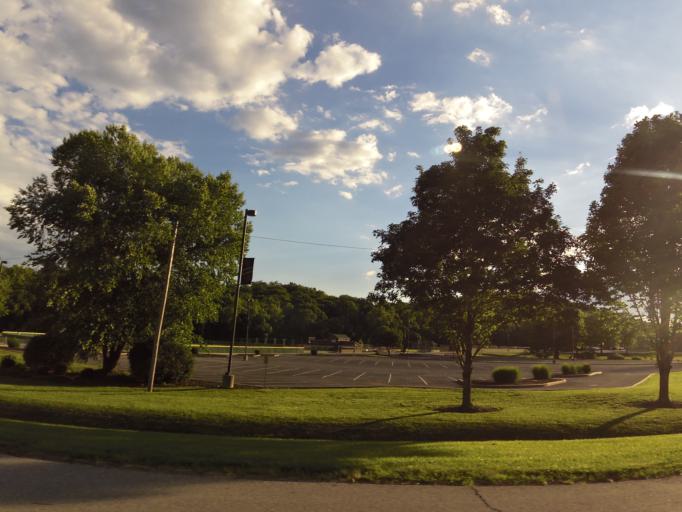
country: US
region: Missouri
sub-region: Saint Louis County
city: Eureka
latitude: 38.5150
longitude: -90.6255
